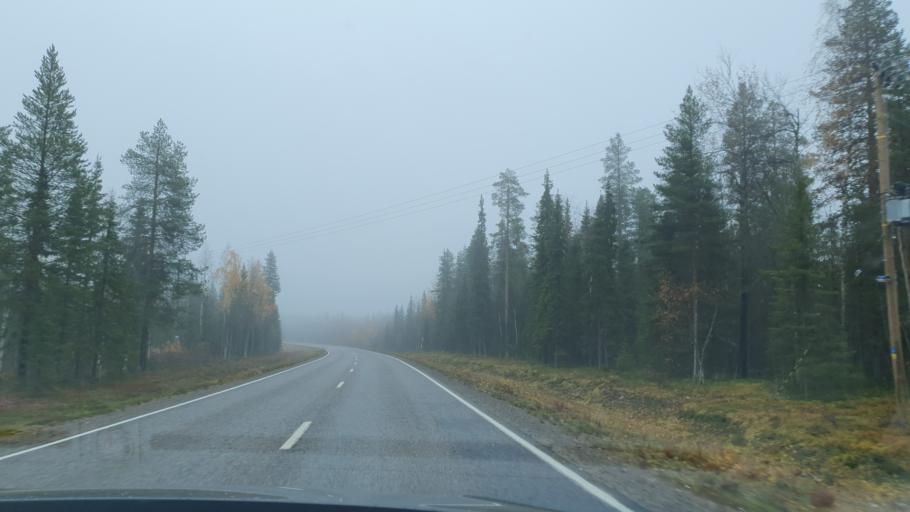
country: FI
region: Lapland
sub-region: Tunturi-Lappi
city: Kittilae
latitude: 67.6612
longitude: 24.8210
